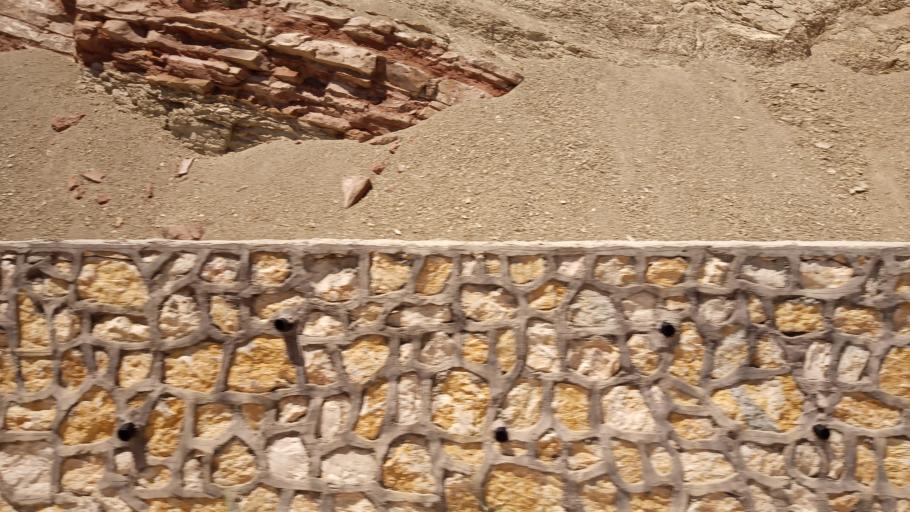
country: TR
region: Malatya
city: Darende
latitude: 38.6078
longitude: 37.4678
